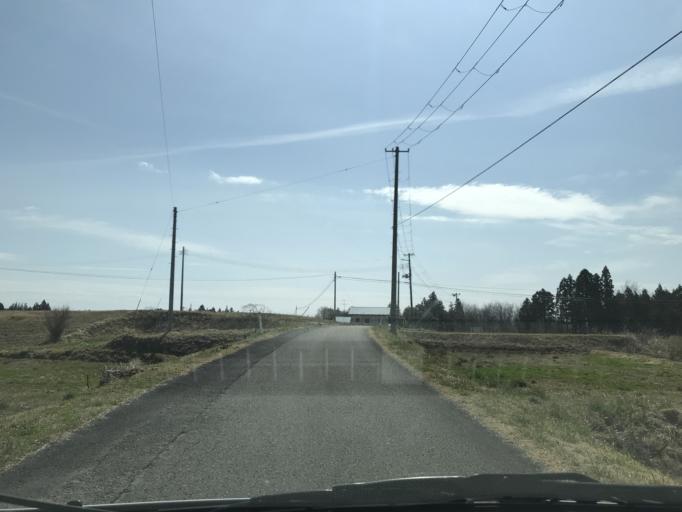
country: JP
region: Iwate
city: Ichinoseki
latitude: 38.8402
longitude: 141.1019
